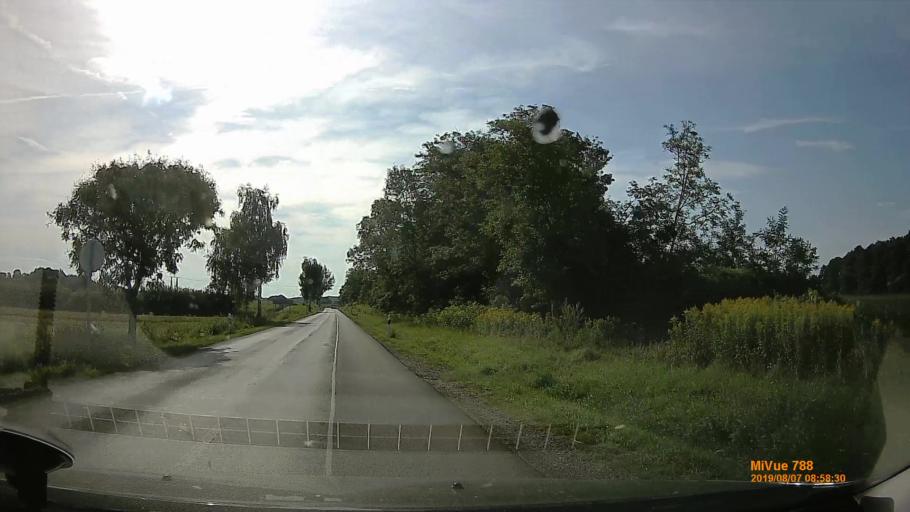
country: HU
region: Zala
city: Pacsa
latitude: 46.7428
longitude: 16.9249
